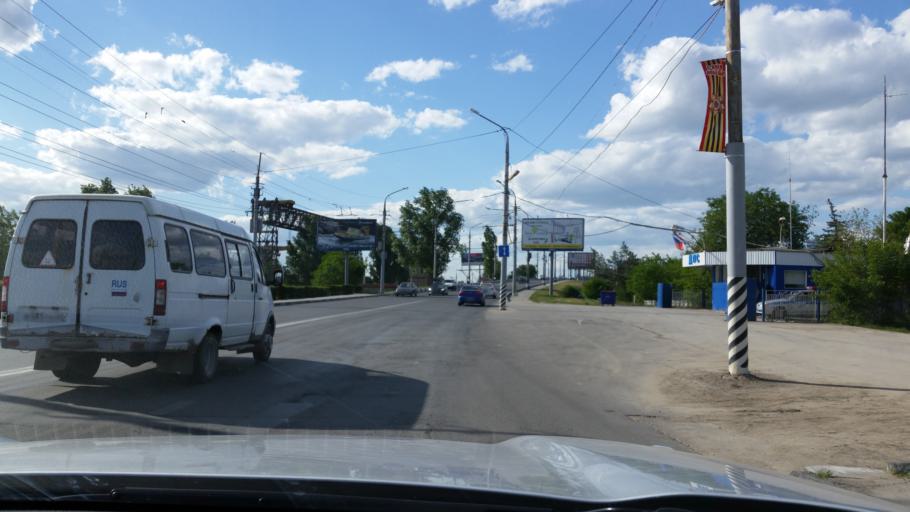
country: RU
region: Saratov
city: Engel's
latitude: 51.5030
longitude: 46.0802
